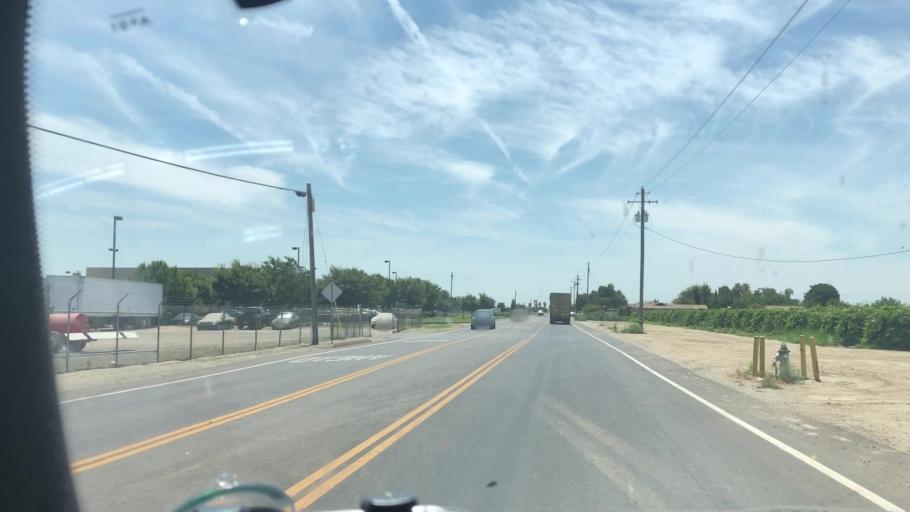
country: US
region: California
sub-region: Fresno County
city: Easton
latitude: 36.6758
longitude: -119.7547
